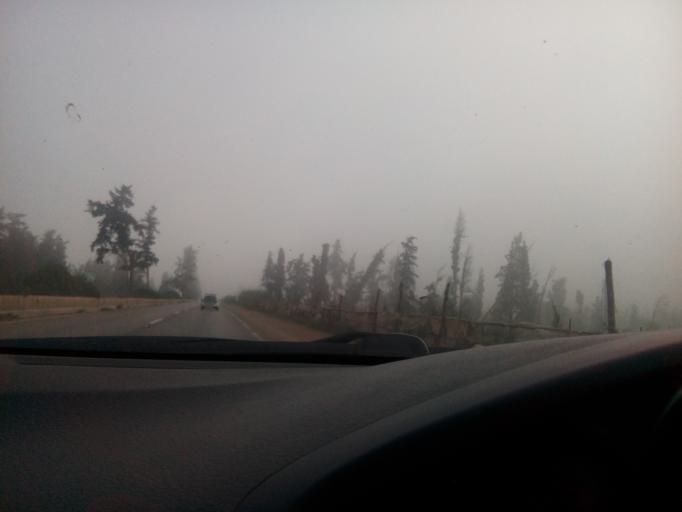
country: DZ
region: Oran
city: Bou Tlelis
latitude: 35.5861
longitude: -0.8128
